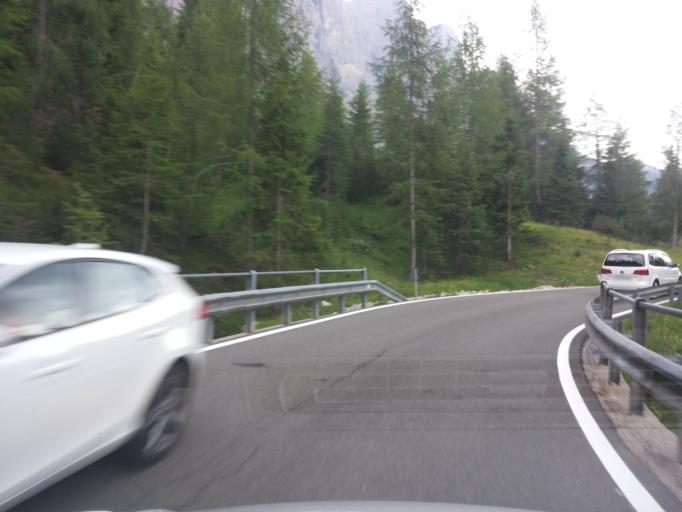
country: IT
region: Trentino-Alto Adige
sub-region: Bolzano
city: Selva
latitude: 46.5273
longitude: 11.7801
